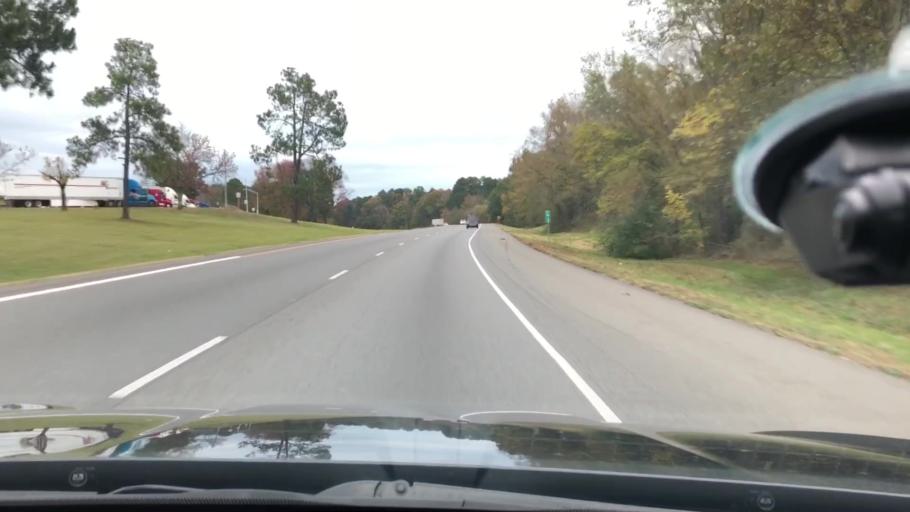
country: US
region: Arkansas
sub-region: Hot Spring County
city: Malvern
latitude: 34.3497
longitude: -92.8927
